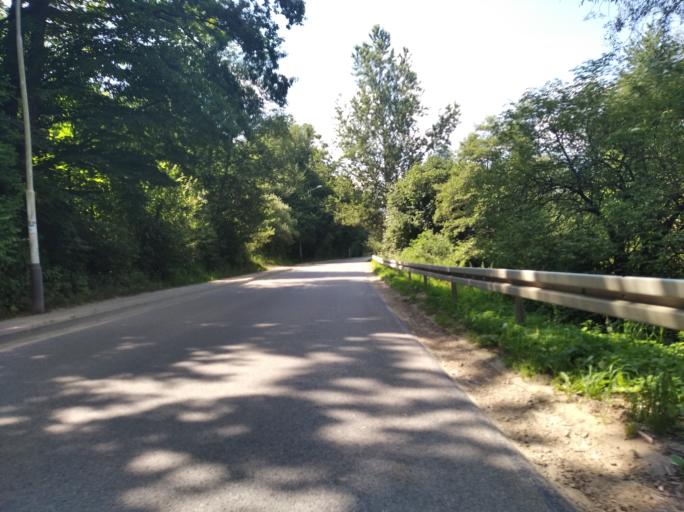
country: PL
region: Subcarpathian Voivodeship
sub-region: Powiat rzeszowski
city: Dynow
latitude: 49.7978
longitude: 22.2443
